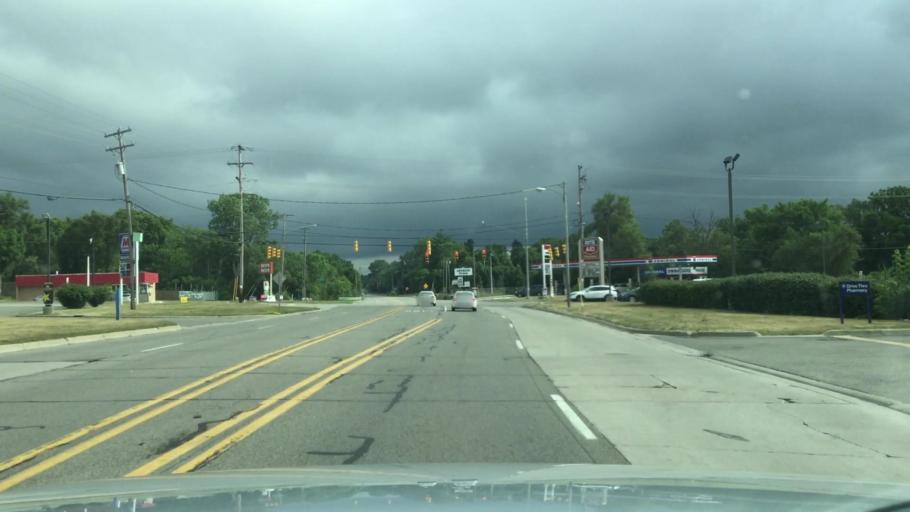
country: US
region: Michigan
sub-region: Genesee County
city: Burton
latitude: 43.0522
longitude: -83.6159
